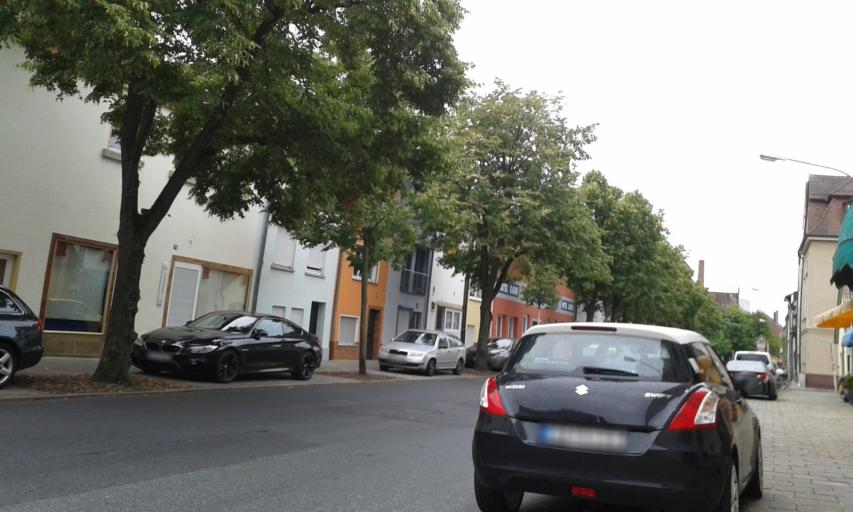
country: DE
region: Bavaria
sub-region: Upper Franconia
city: Bamberg
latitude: 49.8916
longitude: 10.9079
